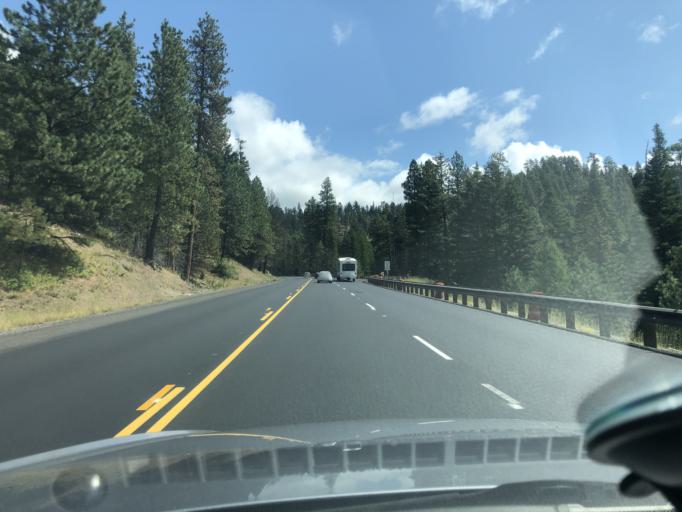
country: US
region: Washington
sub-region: Chelan County
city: Cashmere
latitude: 47.3319
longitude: -120.6038
